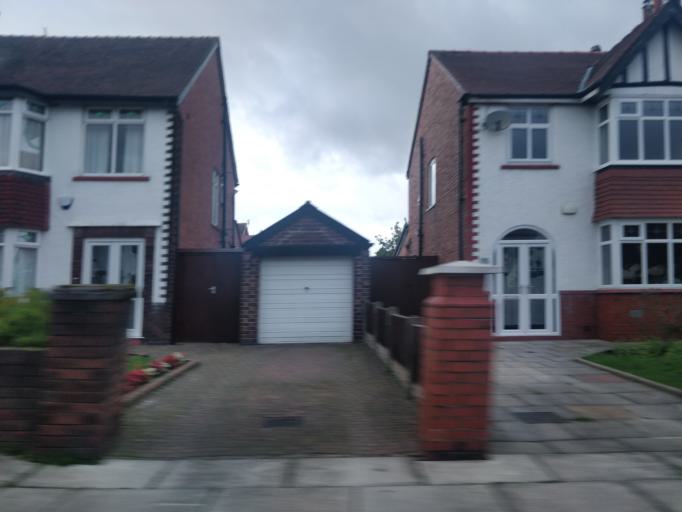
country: GB
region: England
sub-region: Sefton
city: Southport
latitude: 53.6679
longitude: -2.9628
